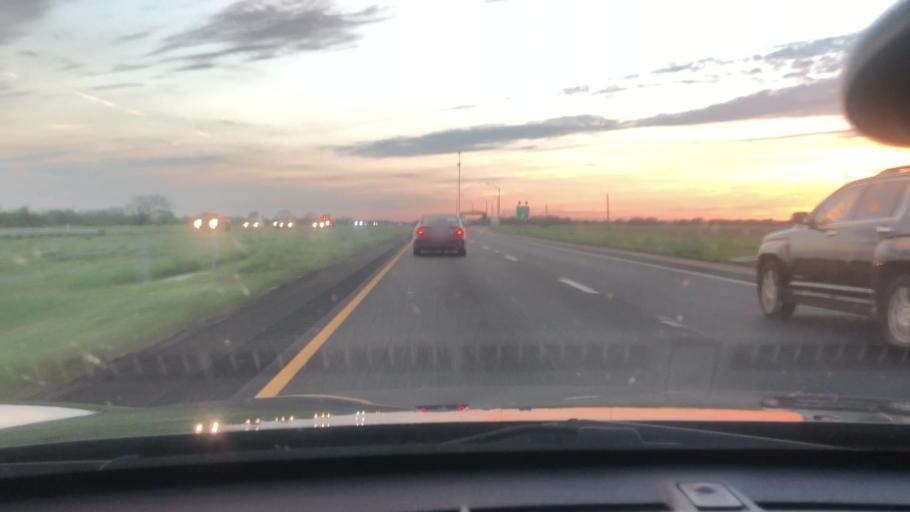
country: US
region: Texas
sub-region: Victoria County
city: Inez
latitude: 28.9284
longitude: -96.7460
